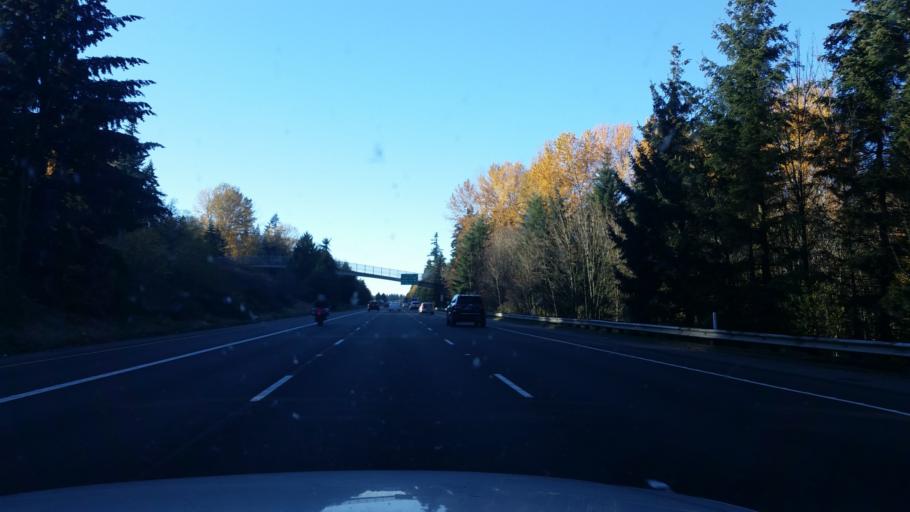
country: US
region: Washington
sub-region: King County
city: West Lake Sammamish
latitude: 47.5698
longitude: -122.1082
